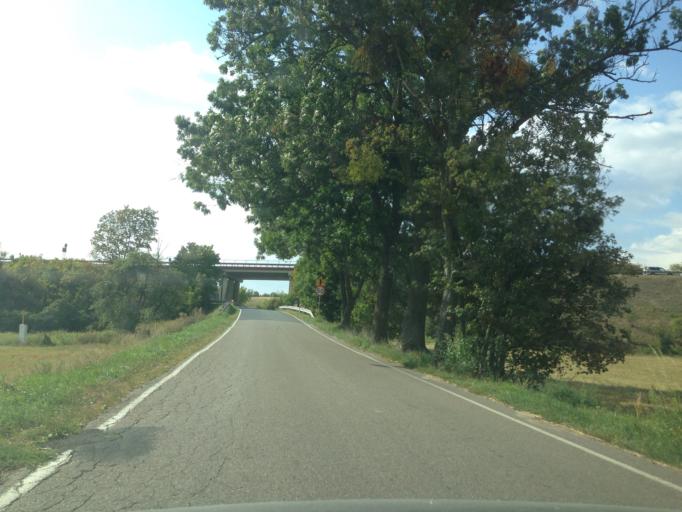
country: PL
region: Kujawsko-Pomorskie
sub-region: Powiat swiecki
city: Bukowiec
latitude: 53.3547
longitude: 18.3072
